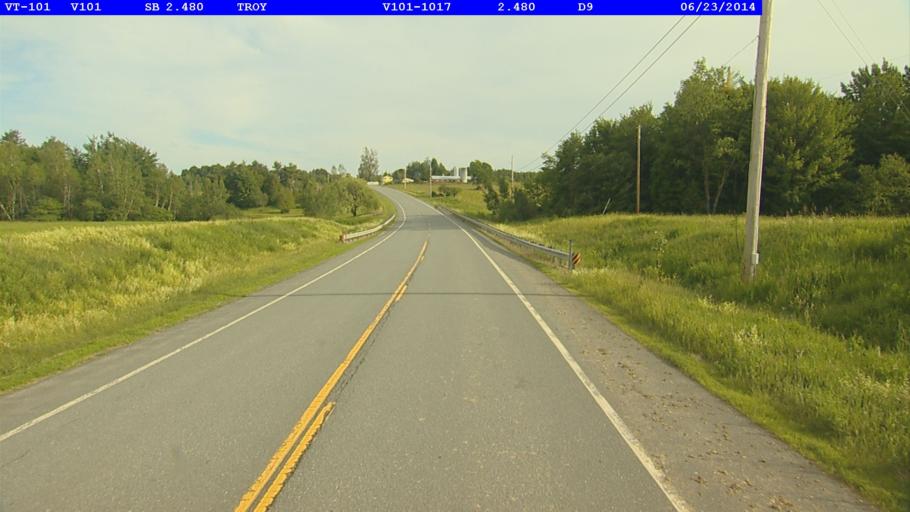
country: US
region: Vermont
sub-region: Orleans County
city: Newport
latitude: 44.9383
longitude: -72.4122
